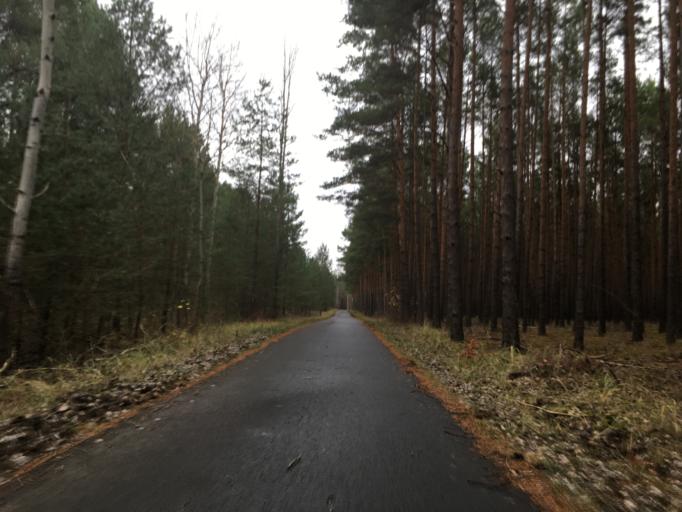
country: DE
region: Brandenburg
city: Mullrose
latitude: 52.2282
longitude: 14.4455
